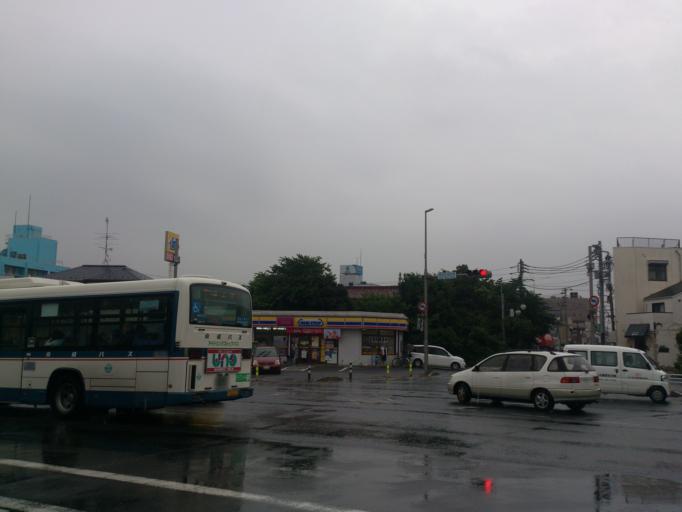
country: JP
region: Chiba
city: Chiba
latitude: 35.6365
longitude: 140.1084
